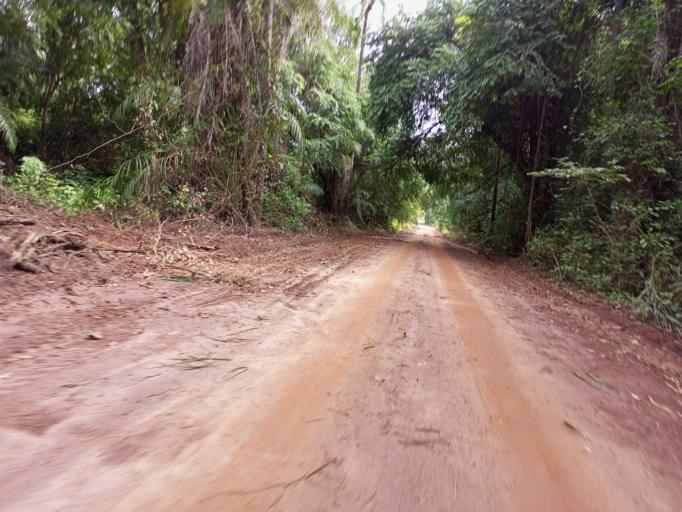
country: GW
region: Oio
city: Bissora
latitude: 12.3966
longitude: -15.6118
